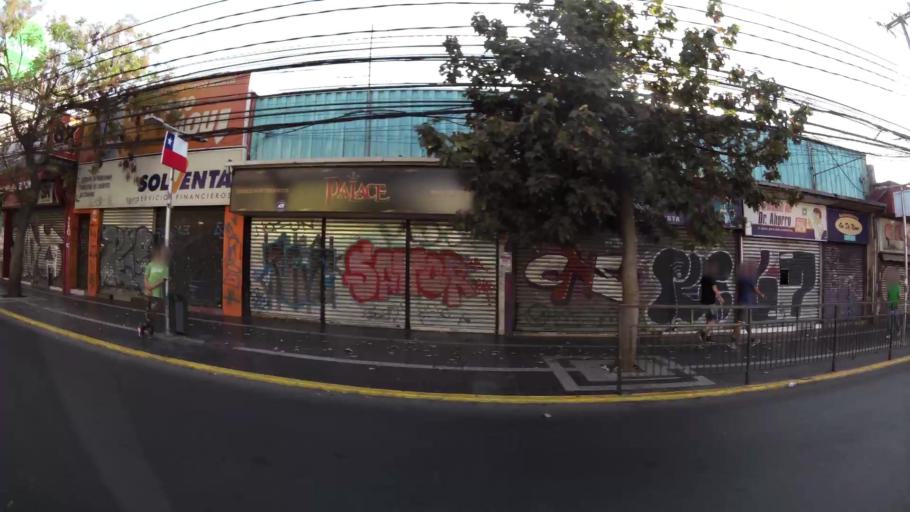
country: CL
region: Santiago Metropolitan
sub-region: Provincia de Cordillera
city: Puente Alto
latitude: -33.6115
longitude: -70.5756
